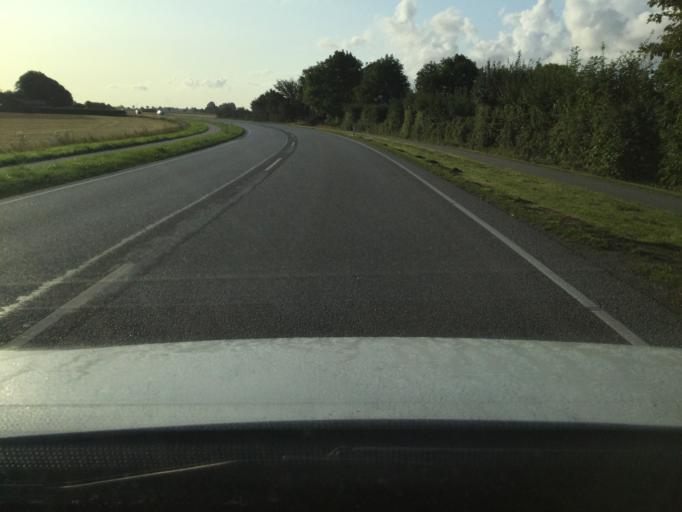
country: DK
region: Zealand
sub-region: Lolland Kommune
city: Nakskov
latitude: 54.8144
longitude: 11.1618
